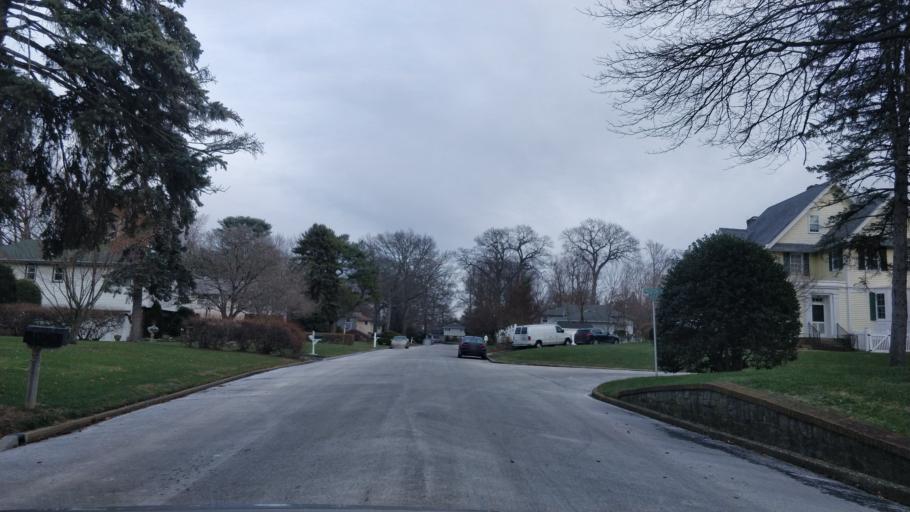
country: US
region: New York
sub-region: Nassau County
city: Glen Cove
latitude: 40.8786
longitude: -73.6293
